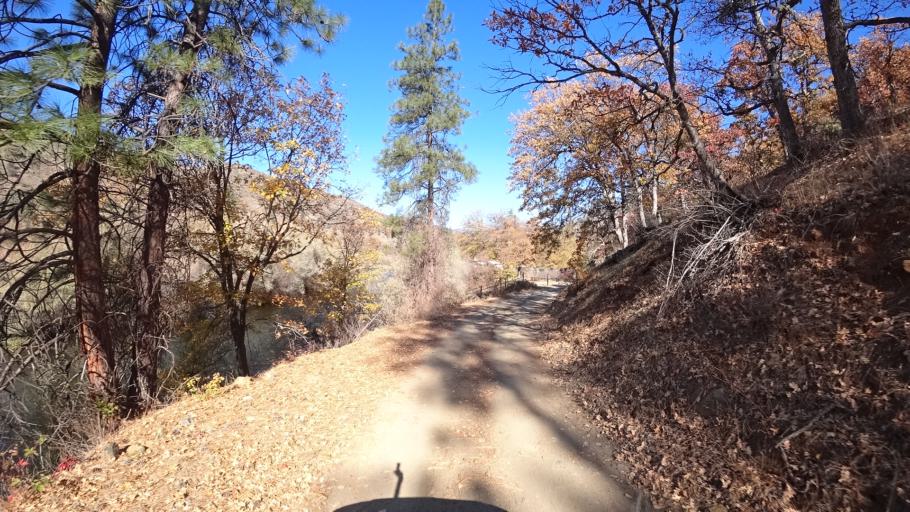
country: US
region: California
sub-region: Siskiyou County
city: Yreka
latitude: 41.8631
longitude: -122.8179
